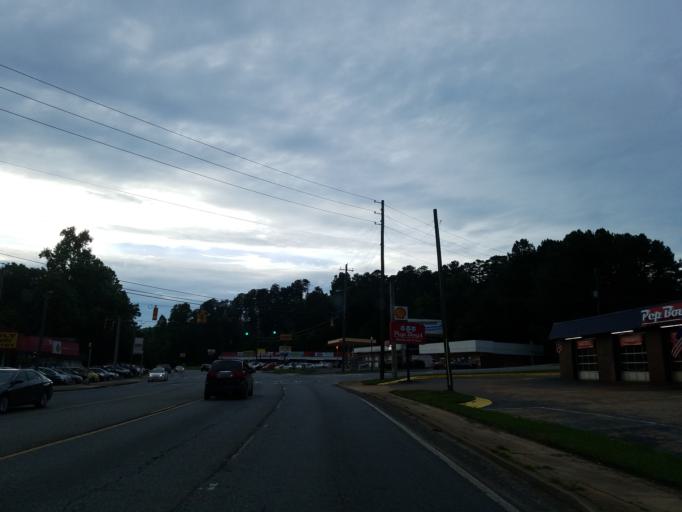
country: US
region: Georgia
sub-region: Forsyth County
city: Cumming
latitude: 34.2110
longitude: -84.1441
